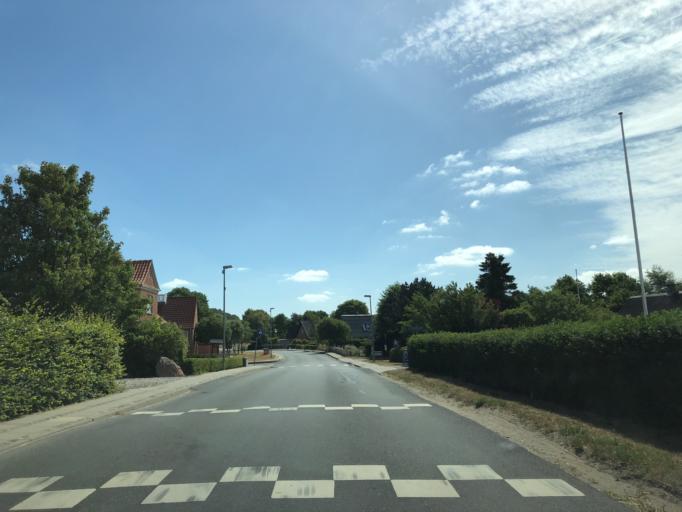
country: DK
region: North Denmark
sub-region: Vesthimmerland Kommune
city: Alestrup
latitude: 56.5797
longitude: 9.5033
